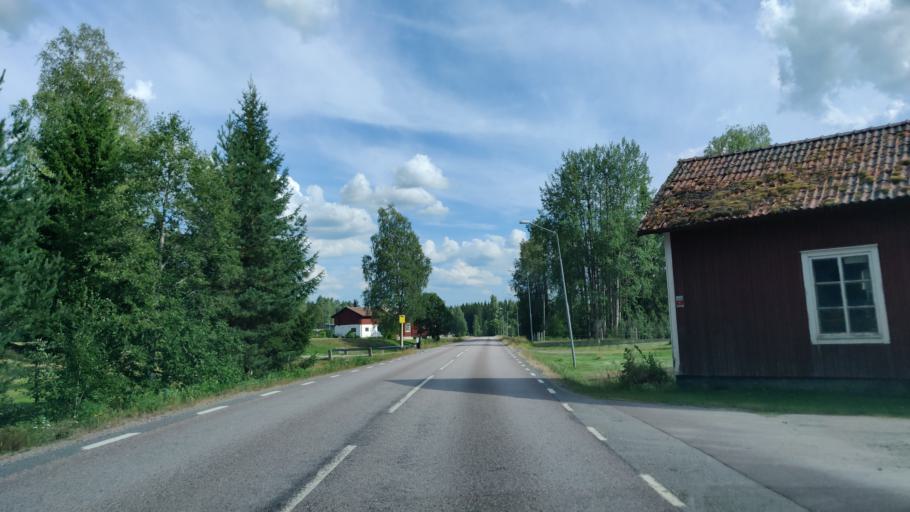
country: SE
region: Vaermland
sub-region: Hagfors Kommun
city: Hagfors
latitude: 60.0720
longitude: 13.6301
